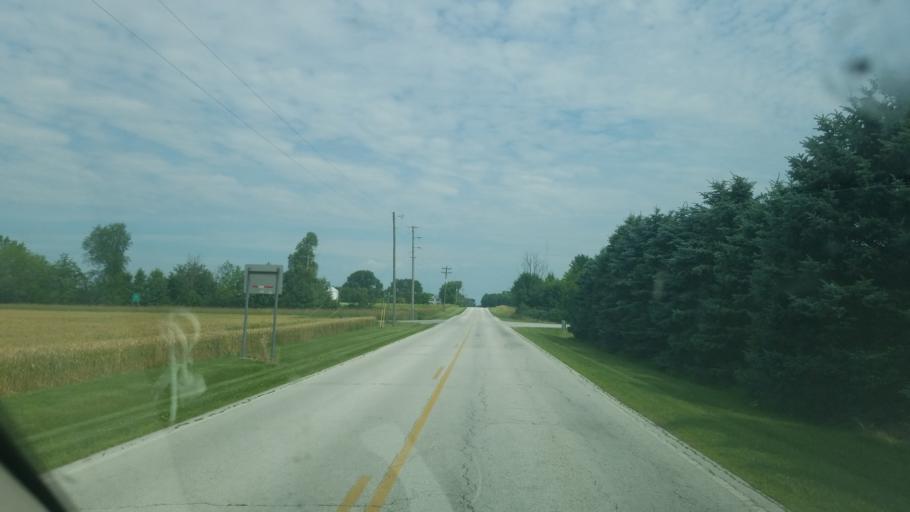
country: US
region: Ohio
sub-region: Seneca County
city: Fostoria
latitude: 41.0928
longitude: -83.4784
